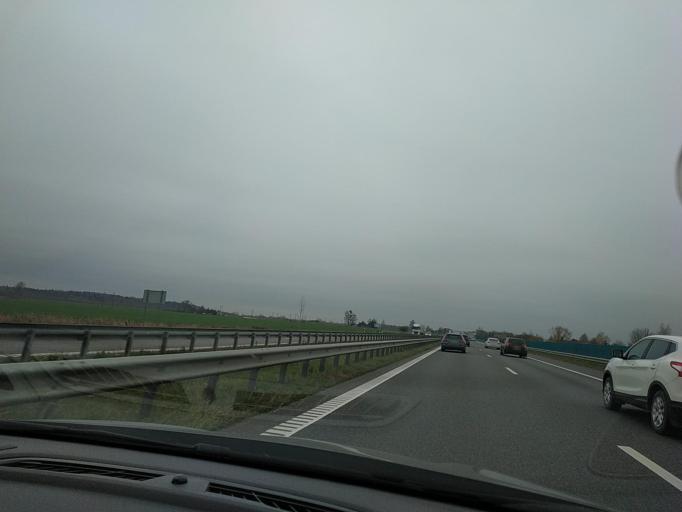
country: LT
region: Kauno apskritis
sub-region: Kauno rajonas
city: Mastaiciai
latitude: 54.7979
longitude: 23.8188
